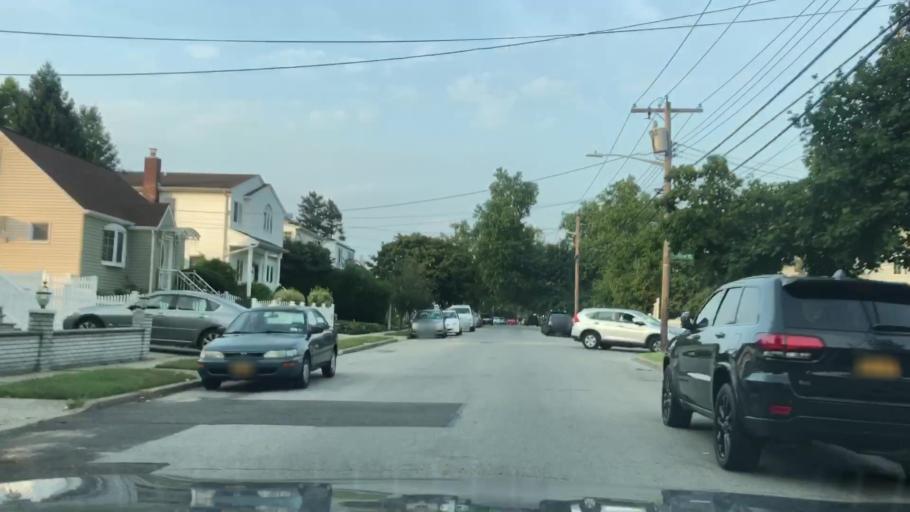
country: US
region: New York
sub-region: Nassau County
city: South Floral Park
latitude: 40.7019
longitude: -73.7002
